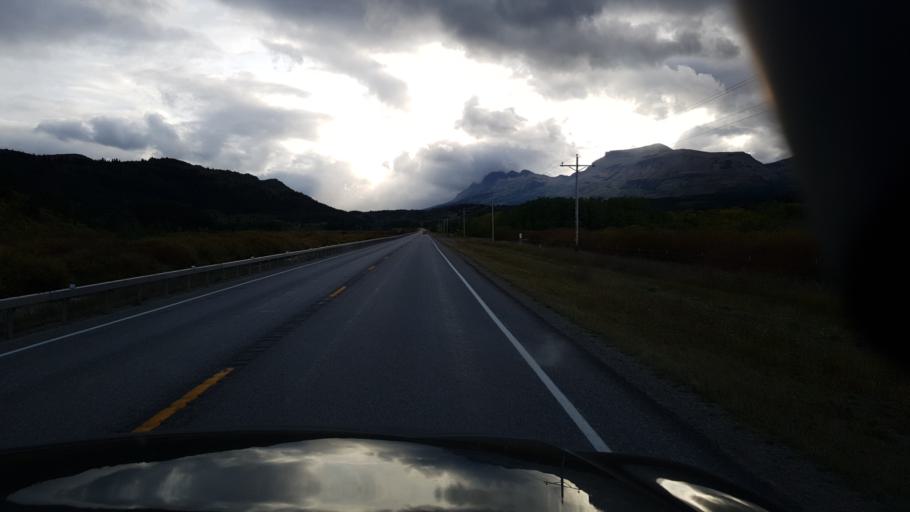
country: US
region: Montana
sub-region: Glacier County
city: South Browning
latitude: 48.4120
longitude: -113.2307
